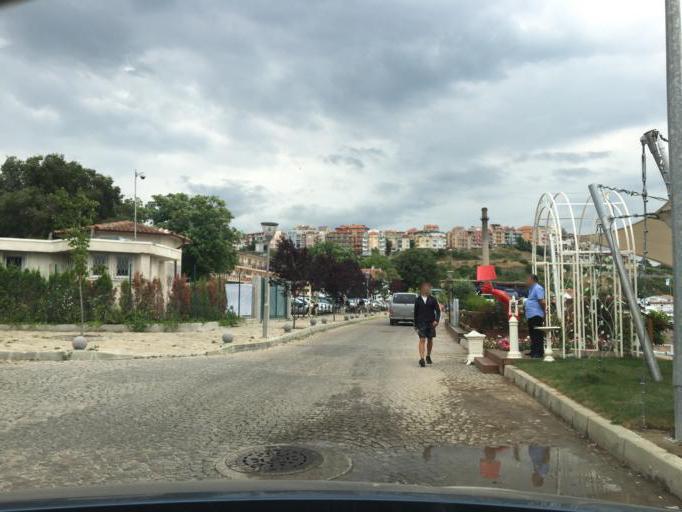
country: BG
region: Burgas
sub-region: Obshtina Sozopol
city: Sozopol
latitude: 42.4215
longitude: 27.6922
